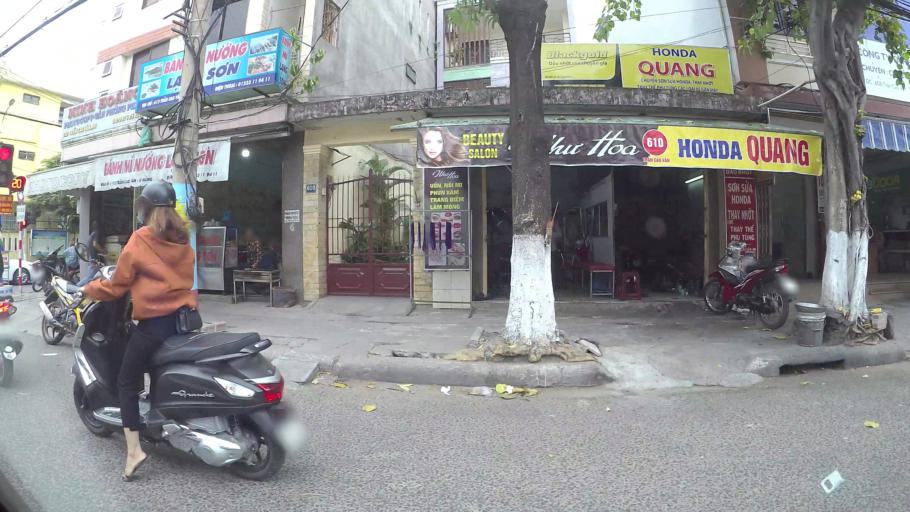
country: VN
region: Da Nang
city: Thanh Khe
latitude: 16.0713
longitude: 108.1920
